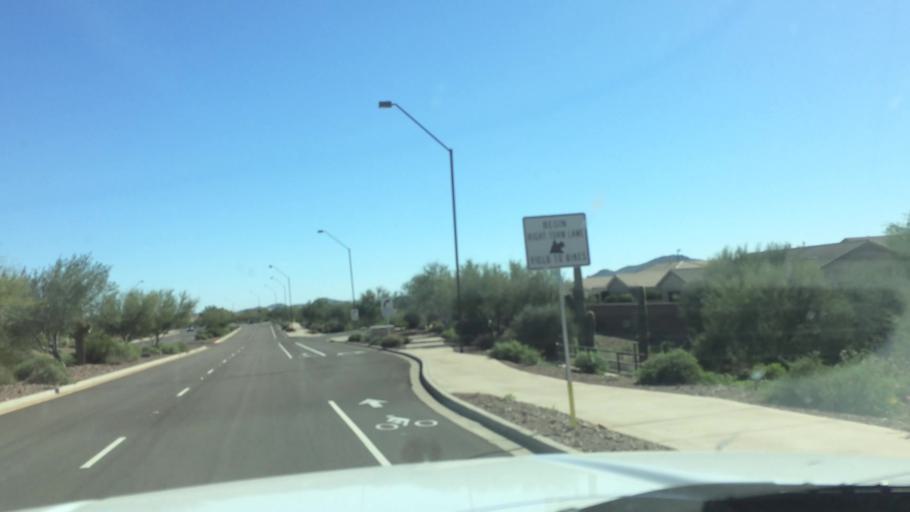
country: US
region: Arizona
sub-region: Maricopa County
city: Anthem
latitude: 33.8552
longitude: -112.1047
